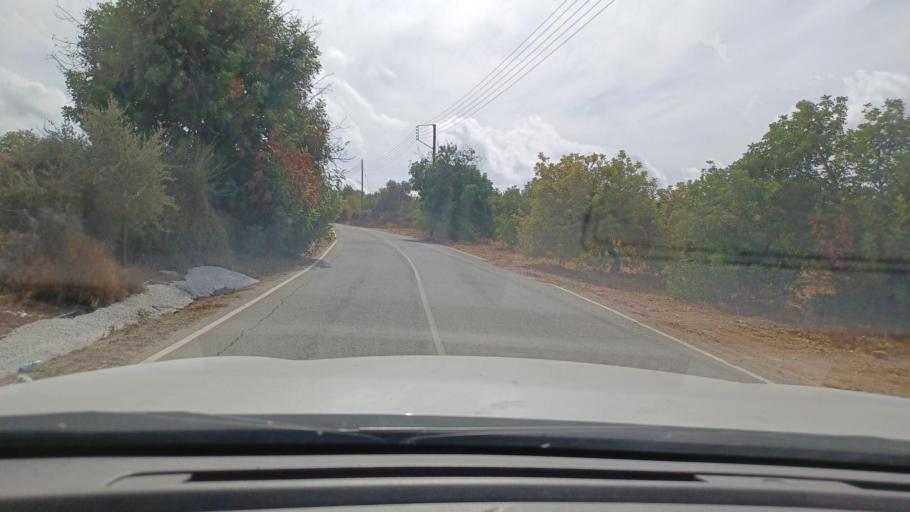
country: CY
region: Pafos
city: Polis
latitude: 34.9472
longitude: 32.4458
